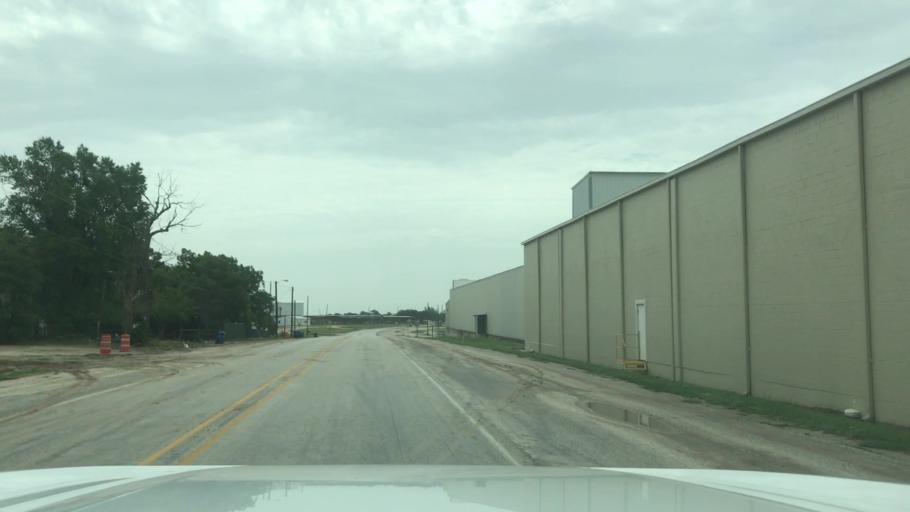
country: US
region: Texas
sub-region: Eastland County
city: Gorman
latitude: 32.2098
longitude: -98.6657
